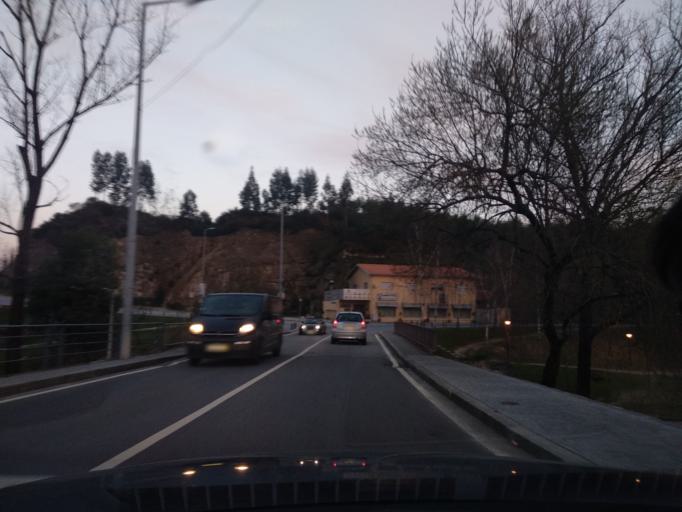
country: PT
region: Porto
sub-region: Paredes
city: Lordelo
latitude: 41.2371
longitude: -8.4126
